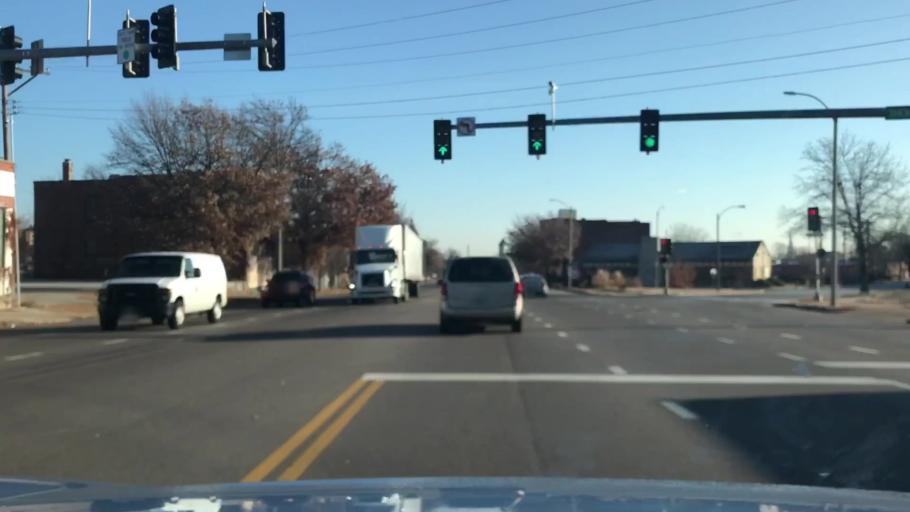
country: US
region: Missouri
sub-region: City of Saint Louis
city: St. Louis
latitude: 38.6069
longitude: -90.2175
